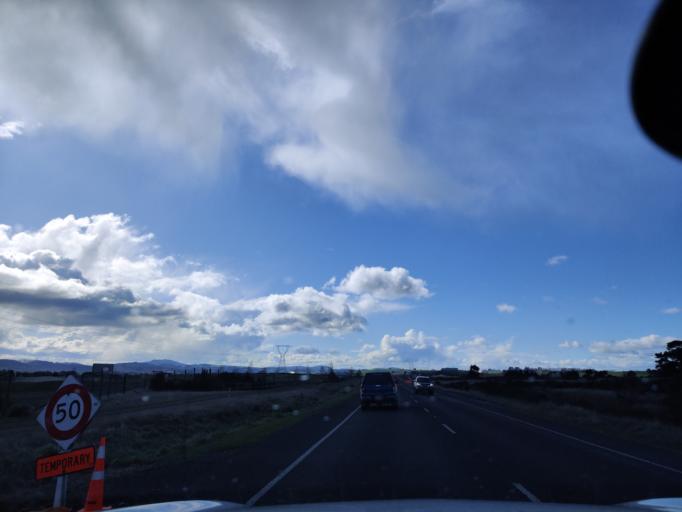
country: NZ
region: Waikato
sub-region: Taupo District
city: Taupo
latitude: -38.6900
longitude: 176.1140
